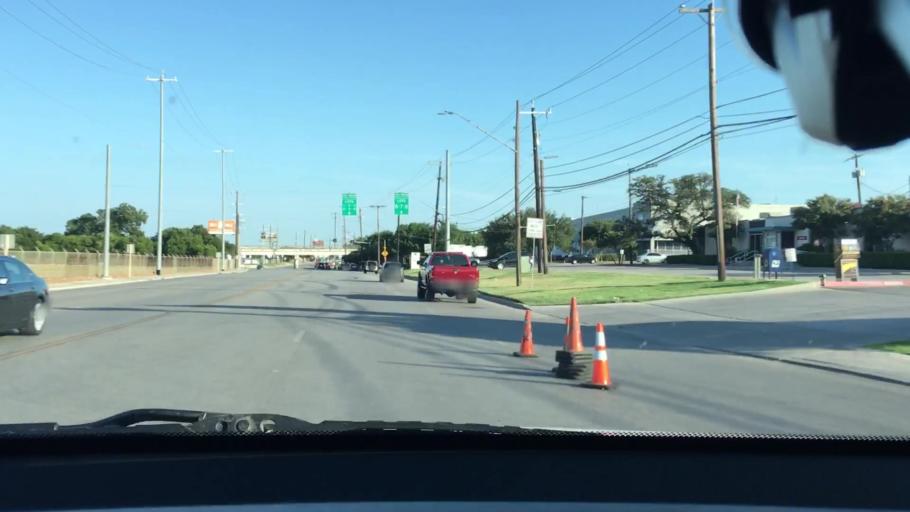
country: US
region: Texas
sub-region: Bexar County
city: Terrell Hills
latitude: 29.4408
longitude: -98.4374
